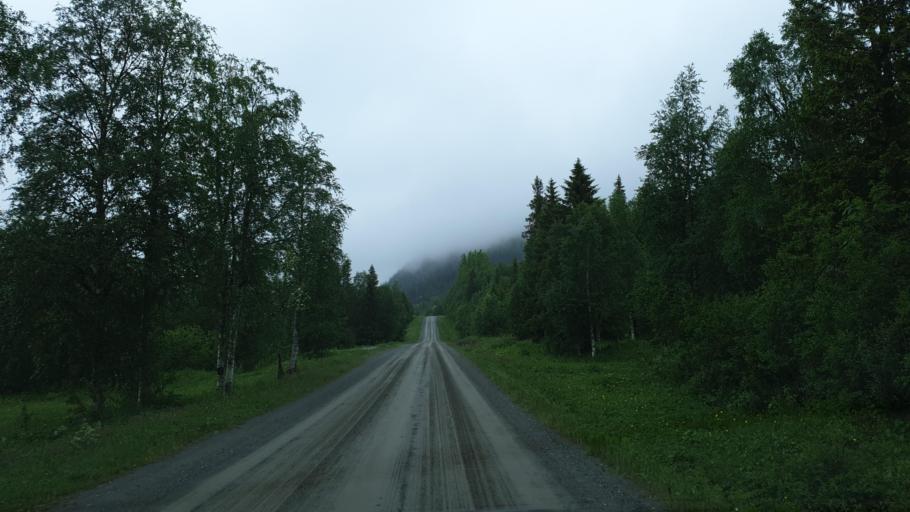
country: SE
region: Vaesterbotten
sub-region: Vilhelmina Kommun
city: Sjoberg
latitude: 65.3429
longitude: 15.8699
